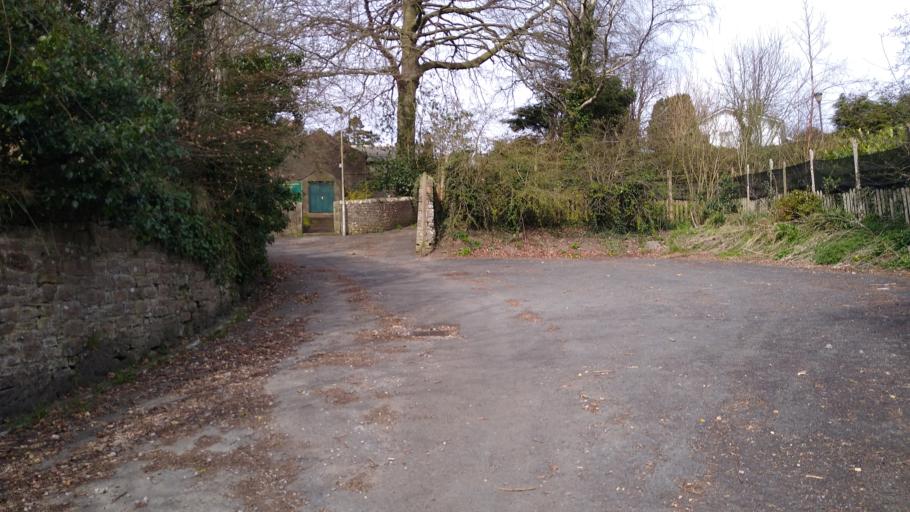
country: GB
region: England
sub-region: Cumbria
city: Dearham
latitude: 54.6704
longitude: -3.4274
